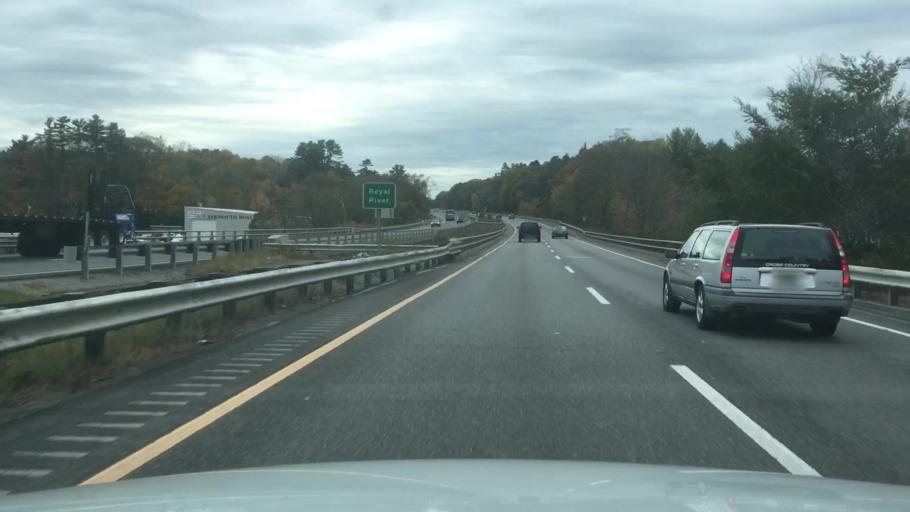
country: US
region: Maine
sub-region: Cumberland County
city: Yarmouth
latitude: 43.7981
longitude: -70.1770
